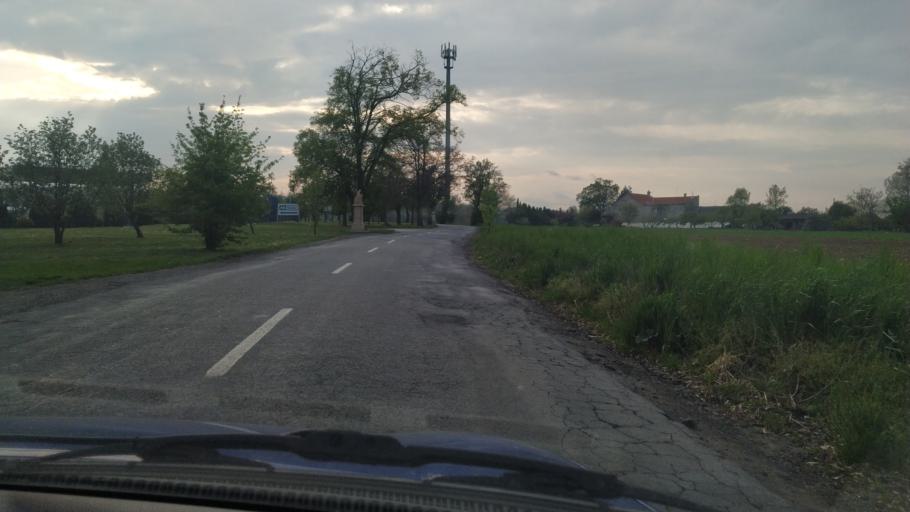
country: CZ
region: Olomoucky
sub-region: Okres Olomouc
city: Slatinice
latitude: 49.5520
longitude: 17.1073
